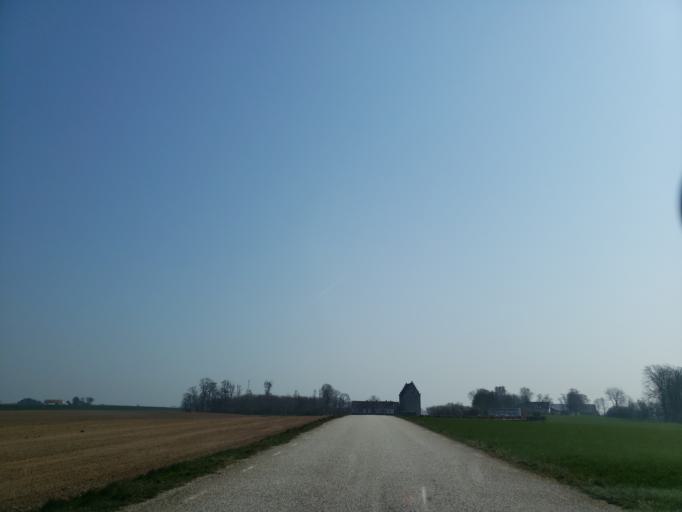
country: SE
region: Skane
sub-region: Simrishamns Kommun
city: Simrishamn
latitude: 55.5023
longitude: 14.2240
